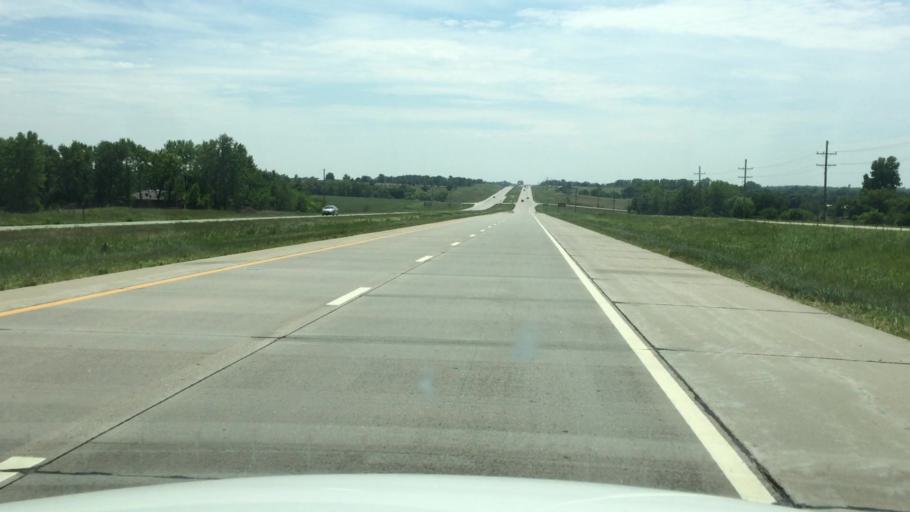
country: US
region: Kansas
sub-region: Jackson County
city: Holton
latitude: 39.3091
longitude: -95.7197
